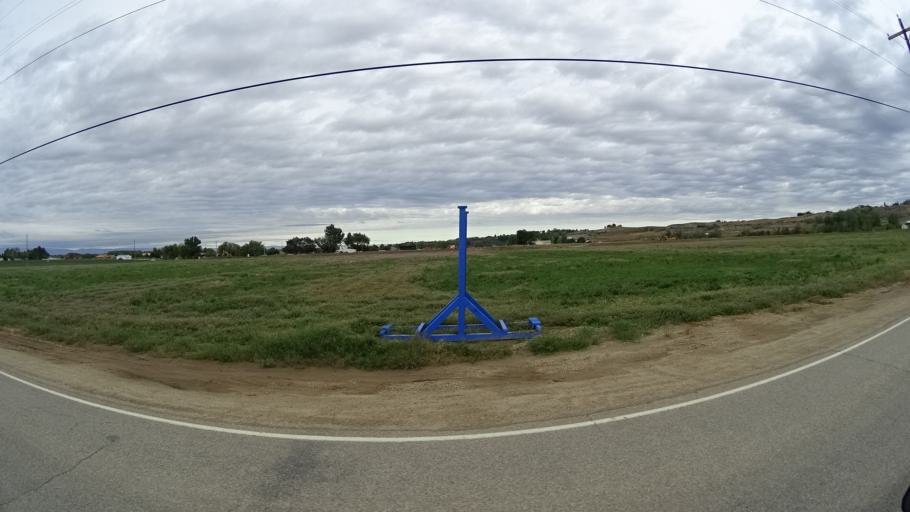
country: US
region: Idaho
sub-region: Ada County
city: Star
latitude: 43.7188
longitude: -116.4831
